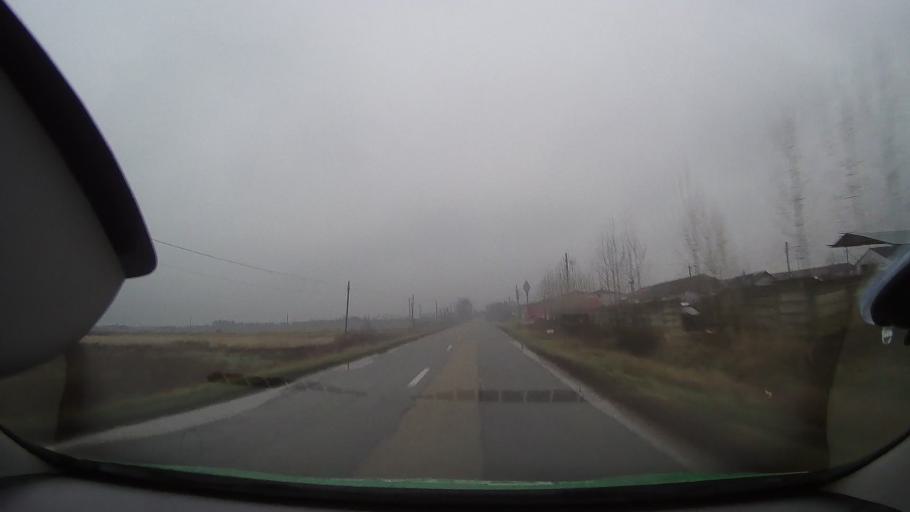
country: RO
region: Bihor
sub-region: Comuna Tulca
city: Tulca
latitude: 46.7926
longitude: 21.7539
